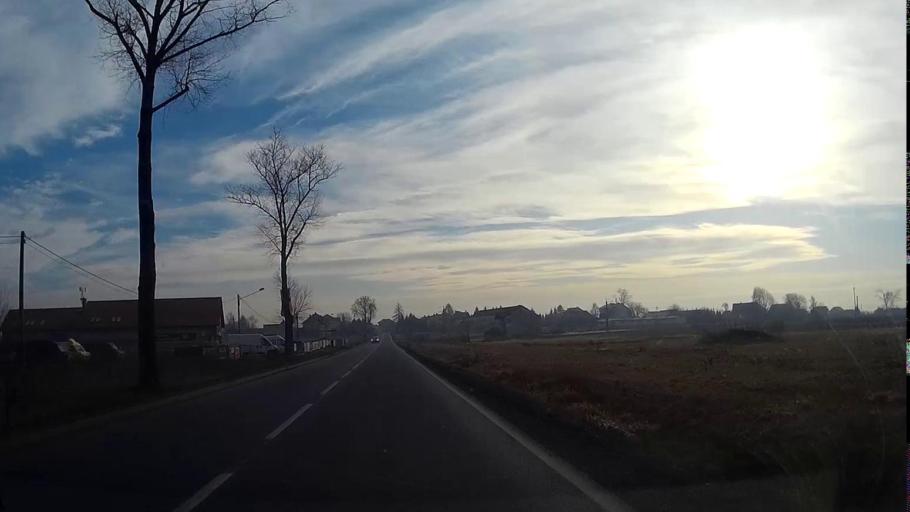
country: PL
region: Lesser Poland Voivodeship
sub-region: Powiat krakowski
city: Liszki
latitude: 50.0355
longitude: 19.7506
